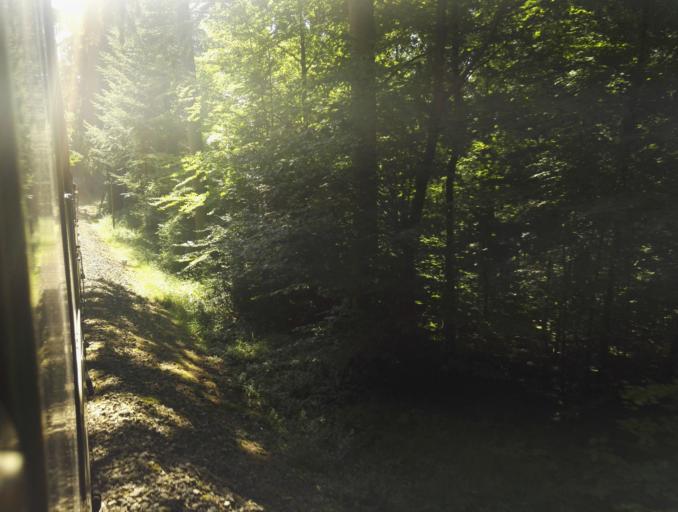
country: DE
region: Baden-Wuerttemberg
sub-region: Regierungsbezirk Stuttgart
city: Welzheim
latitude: 48.8638
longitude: 9.6243
